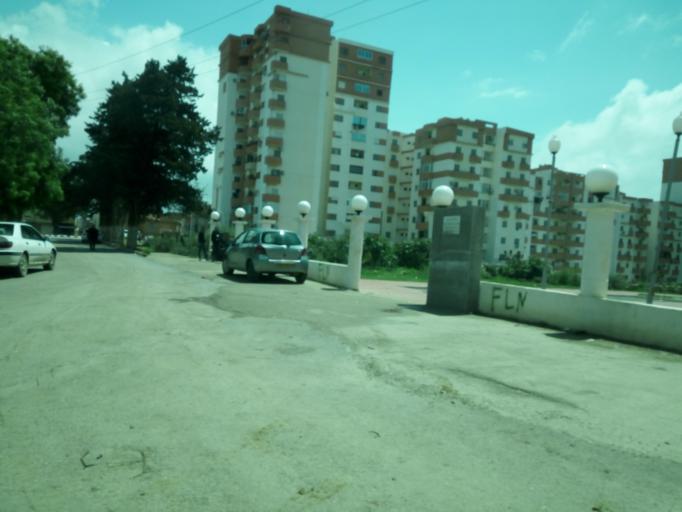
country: DZ
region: Tipaza
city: Saoula
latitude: 36.7297
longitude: 2.9972
